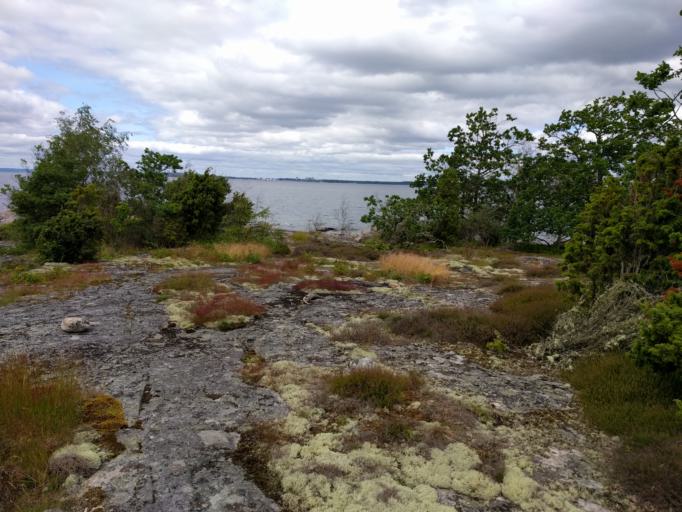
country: SE
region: Blekinge
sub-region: Karlshamns Kommun
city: Karlshamn
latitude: 56.1230
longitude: 14.9544
